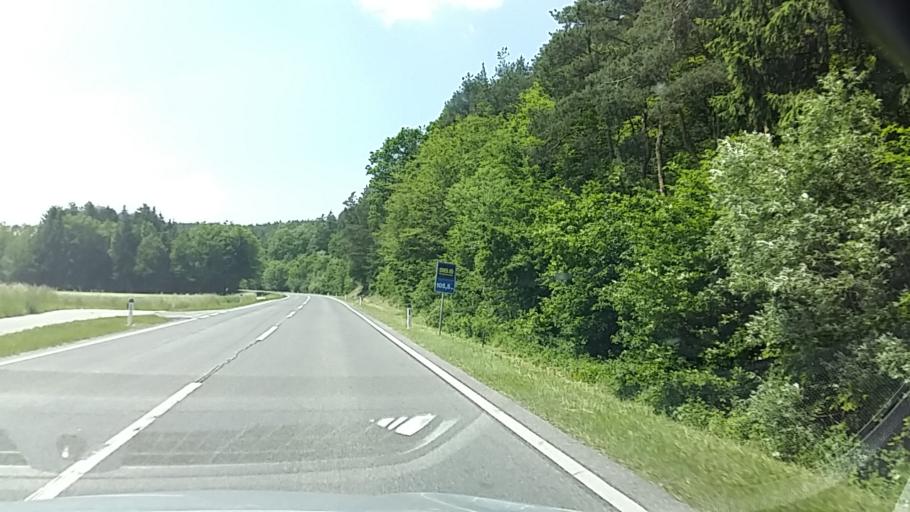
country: AT
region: Burgenland
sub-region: Politischer Bezirk Oberpullendorf
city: Oberpullendorf
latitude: 47.4823
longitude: 16.4631
